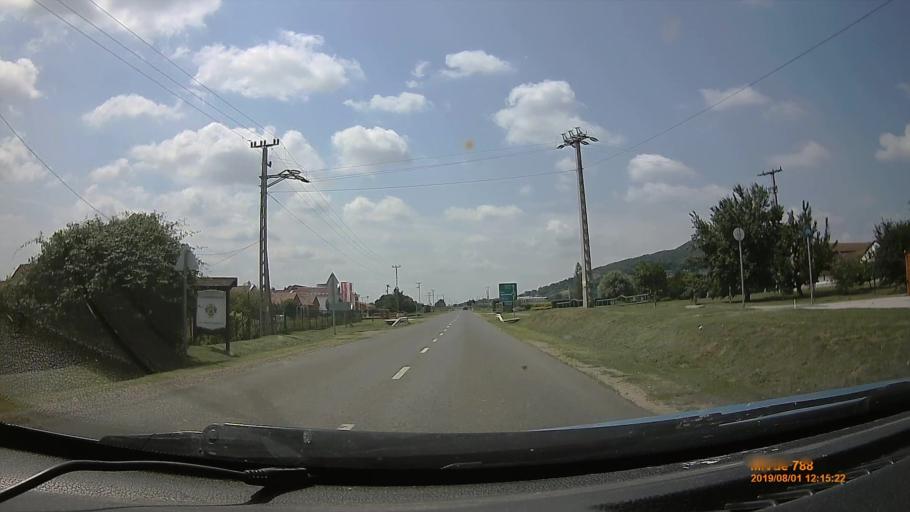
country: HU
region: Baranya
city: Villany
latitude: 45.8642
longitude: 18.4462
